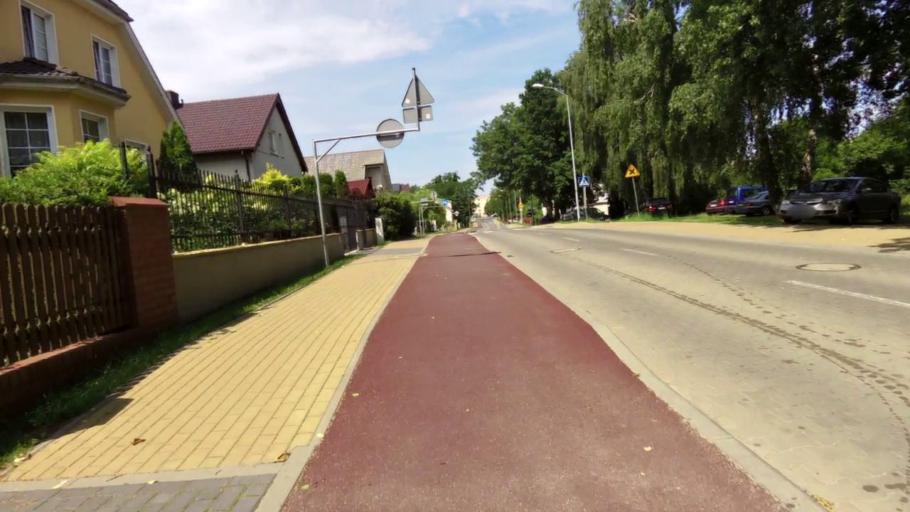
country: PL
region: West Pomeranian Voivodeship
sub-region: Powiat gryfinski
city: Stare Czarnowo
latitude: 53.3721
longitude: 14.6901
